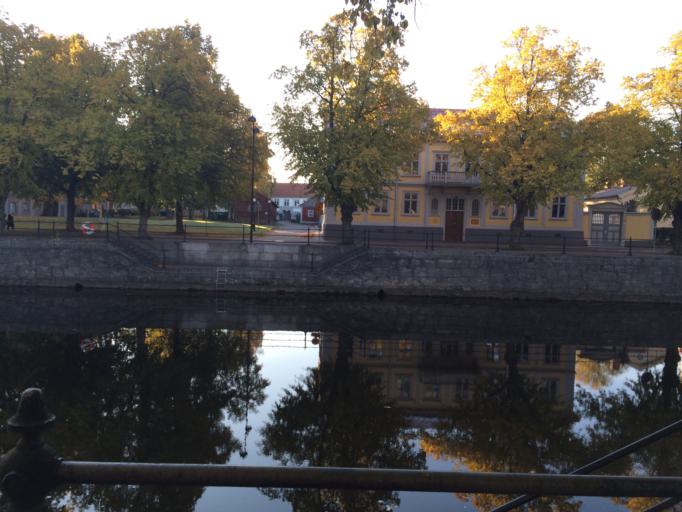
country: SE
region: Gaevleborg
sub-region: Gavle Kommun
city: Gavle
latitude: 60.6743
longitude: 17.1482
